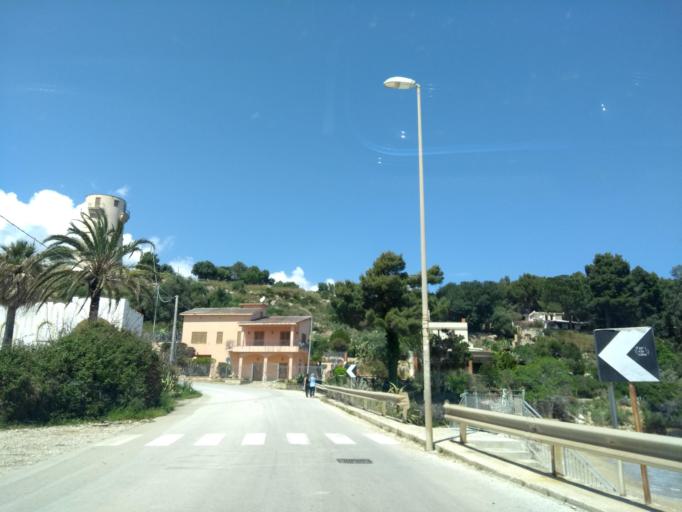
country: IT
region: Sicily
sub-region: Trapani
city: Castellammare del Golfo
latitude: 38.0576
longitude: 12.8390
